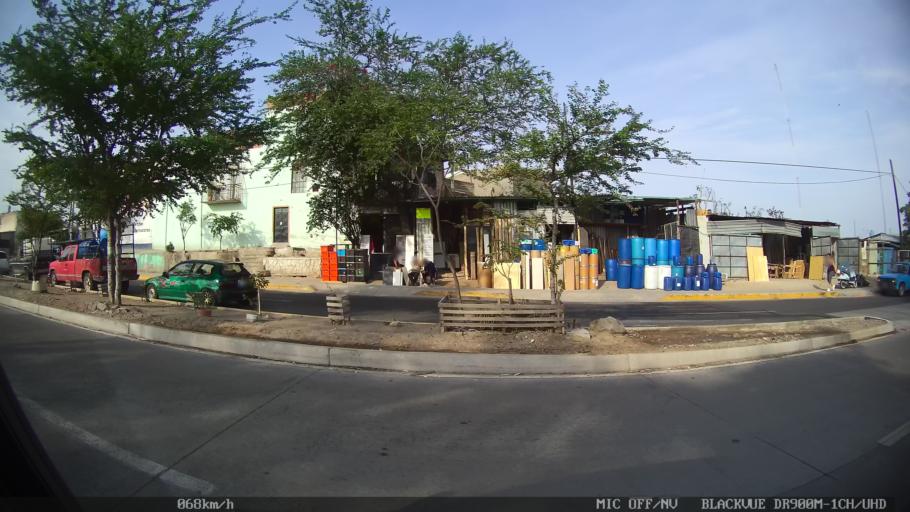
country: MX
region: Jalisco
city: Tlaquepaque
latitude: 20.7025
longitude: -103.2811
